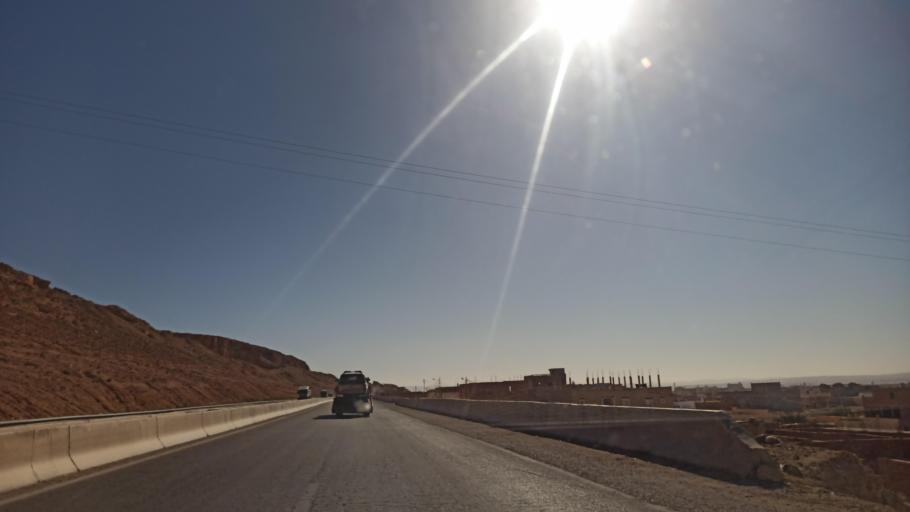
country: TN
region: Gafsa
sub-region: Gafsa Municipality
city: Gafsa
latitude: 34.4402
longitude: 8.7921
